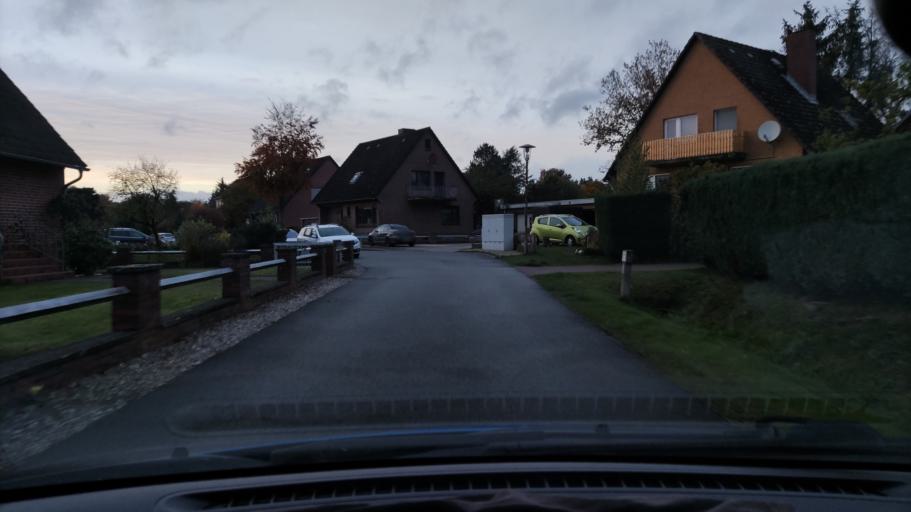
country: DE
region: Lower Saxony
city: Artlenburg
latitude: 53.3672
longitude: 10.4797
